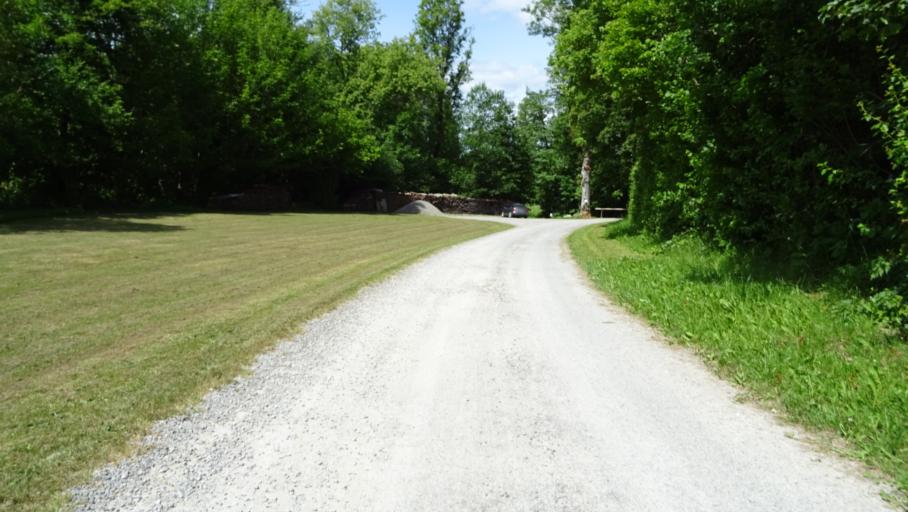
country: DE
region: Baden-Wuerttemberg
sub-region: Karlsruhe Region
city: Seckach
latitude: 49.4731
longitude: 9.3176
